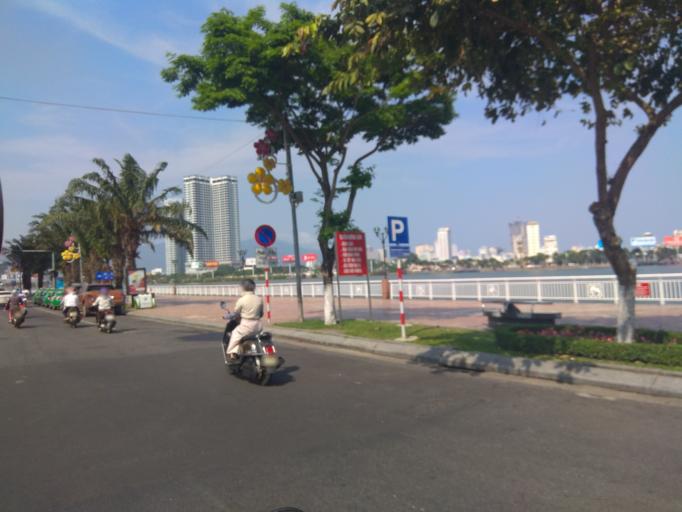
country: VN
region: Da Nang
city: Da Nang
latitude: 16.0660
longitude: 108.2245
